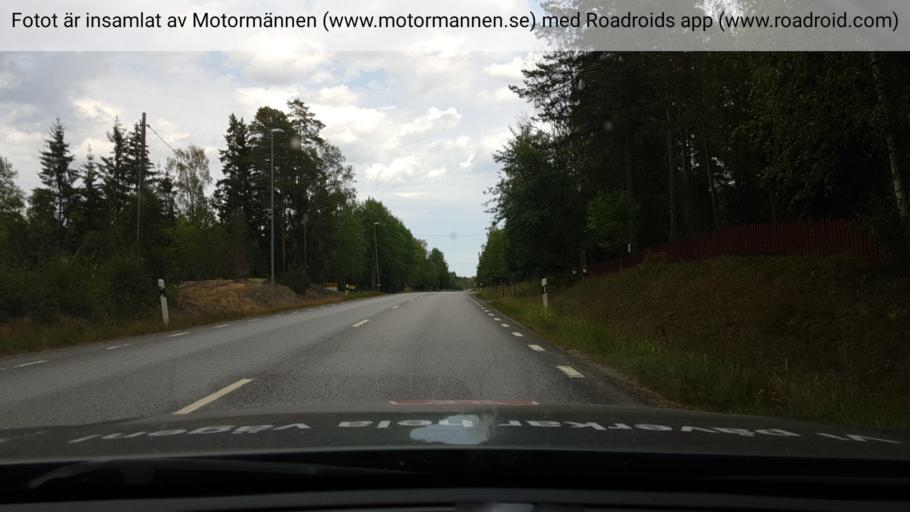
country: SE
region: Uppsala
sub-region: Heby Kommun
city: Morgongava
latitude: 59.8933
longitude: 17.1515
